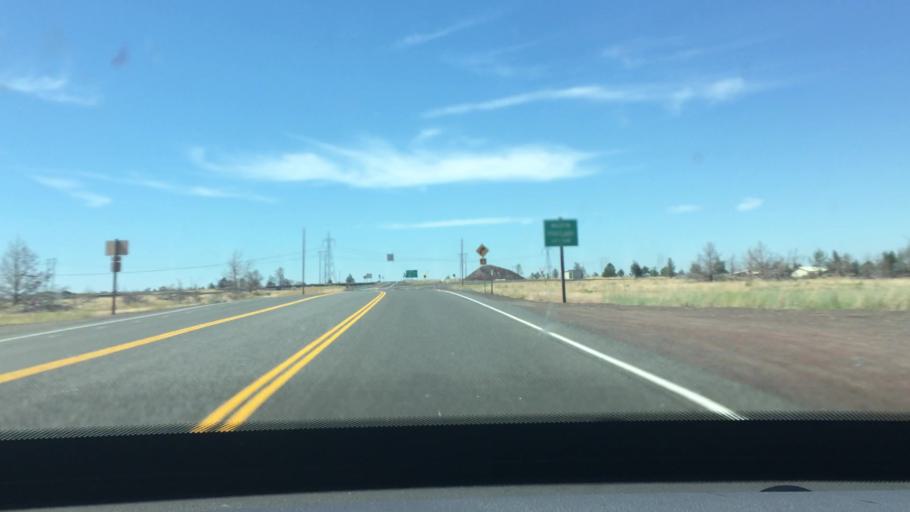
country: US
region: Oregon
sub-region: Jefferson County
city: Madras
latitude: 44.9180
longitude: -120.9442
